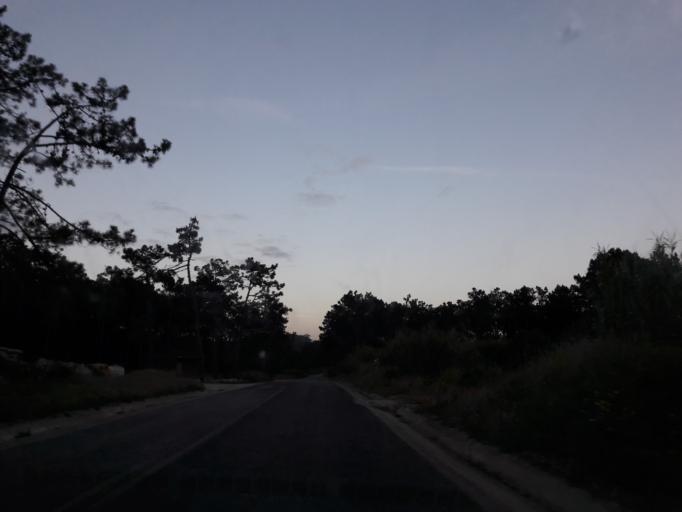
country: PT
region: Leiria
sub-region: Peniche
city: Atouguia da Baleia
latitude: 39.3577
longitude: -9.2989
